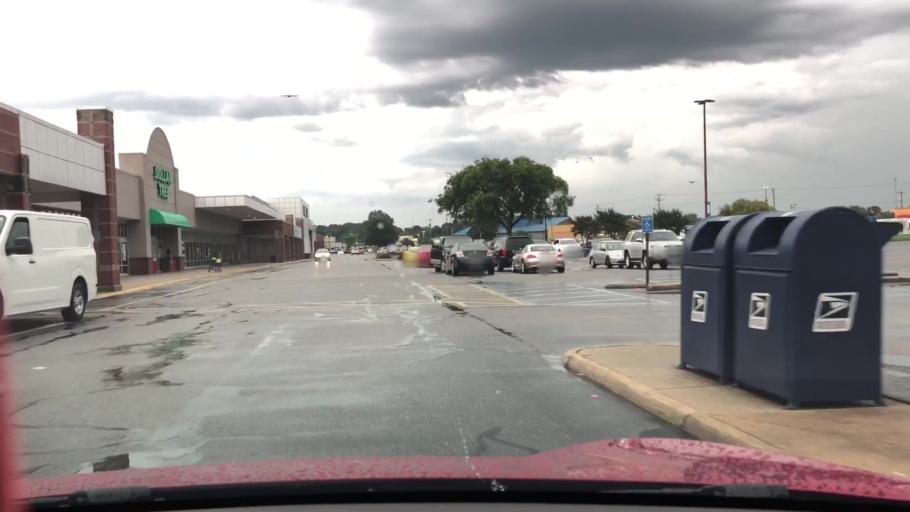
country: US
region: Virginia
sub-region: City of Chesapeake
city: Chesapeake
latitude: 36.8581
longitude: -76.2039
